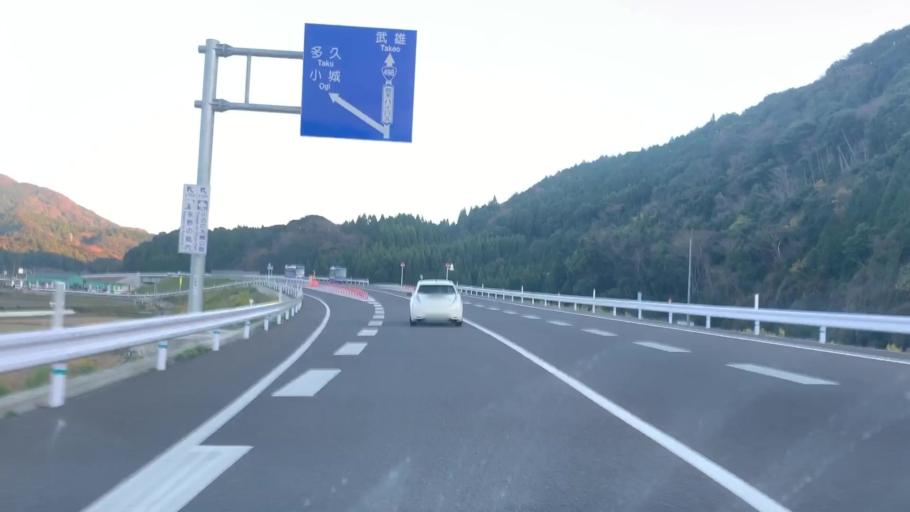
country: JP
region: Saga Prefecture
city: Takeocho-takeo
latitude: 33.2510
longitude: 129.9918
